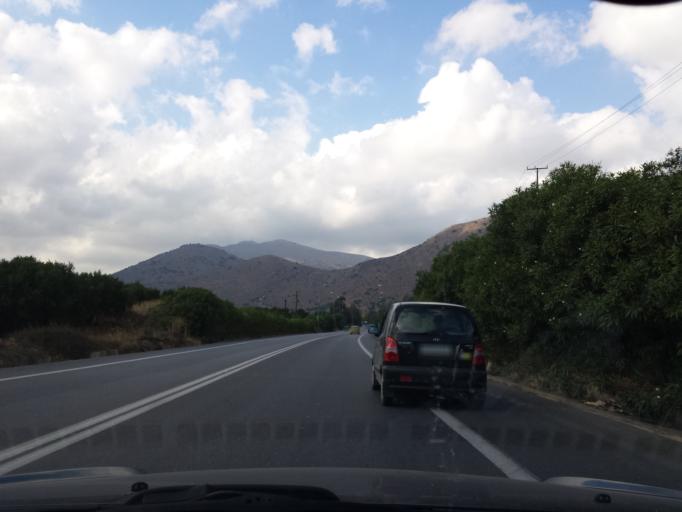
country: GR
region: Crete
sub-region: Nomos Lasithiou
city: Neapoli
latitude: 35.2380
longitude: 25.6473
